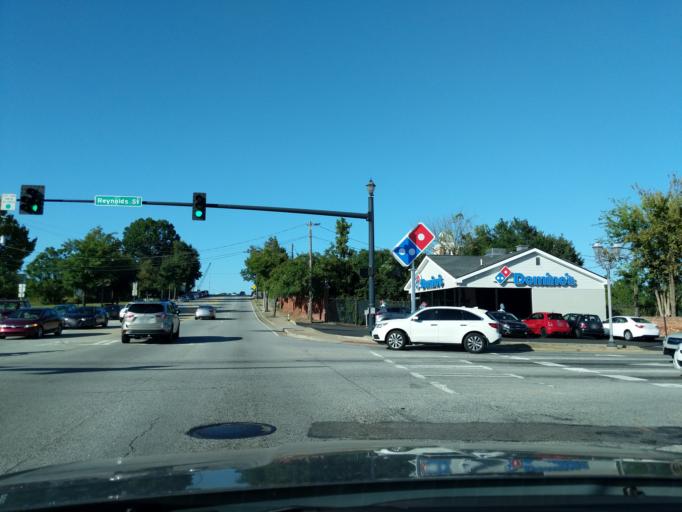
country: US
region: Georgia
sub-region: Richmond County
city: Augusta
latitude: 33.4800
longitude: -81.9748
